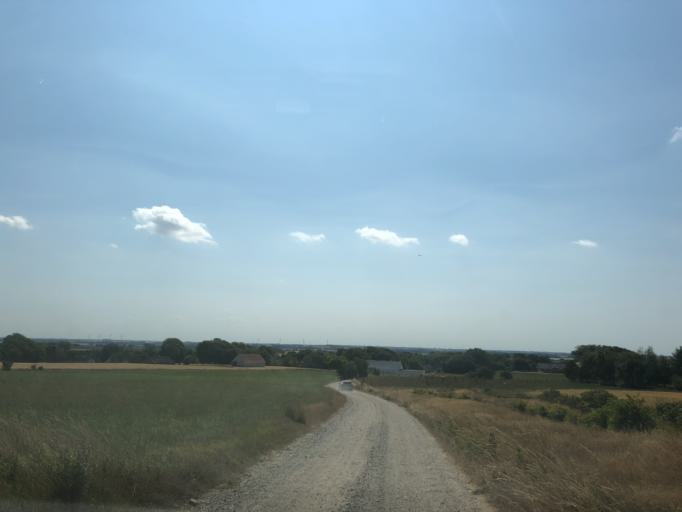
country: DK
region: North Denmark
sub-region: Morso Kommune
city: Nykobing Mors
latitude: 56.8282
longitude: 8.9961
